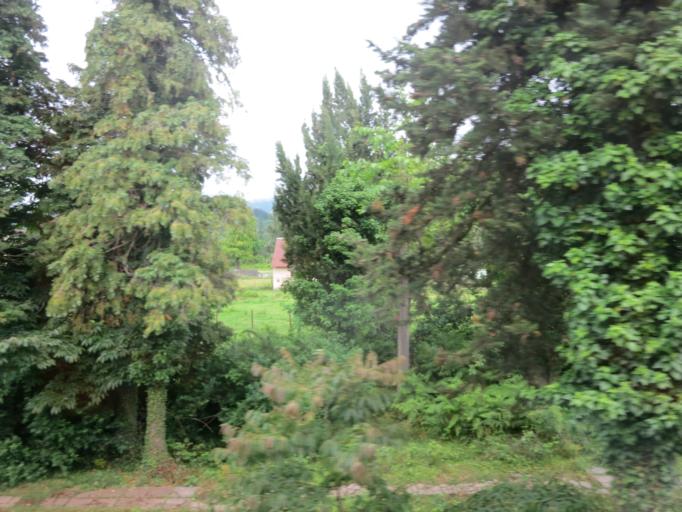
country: GE
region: Ajaria
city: Makhinjauri
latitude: 41.7260
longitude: 41.7302
